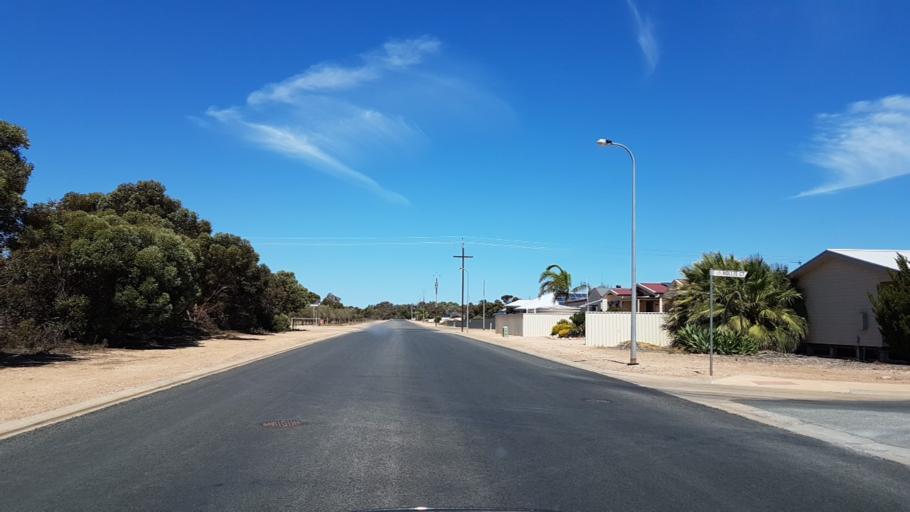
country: AU
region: South Australia
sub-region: Copper Coast
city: Wallaroo
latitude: -34.0557
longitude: 137.5805
